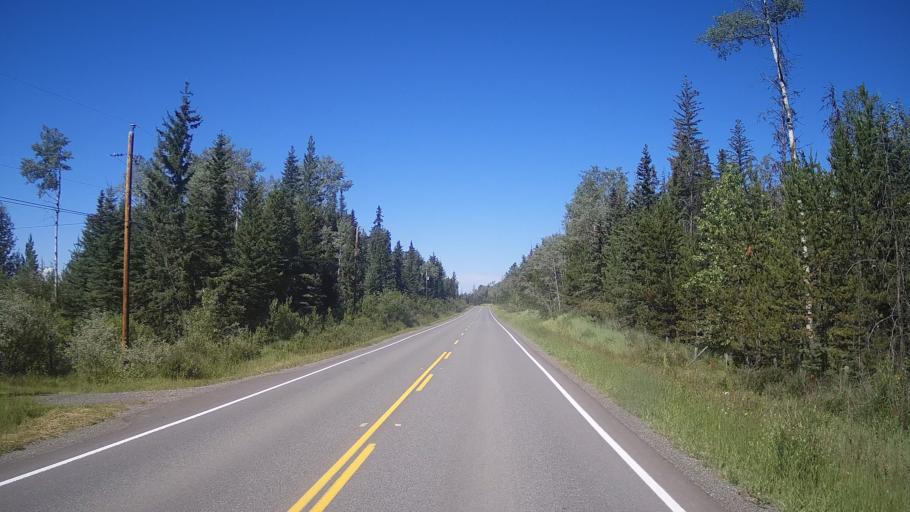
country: CA
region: British Columbia
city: Cache Creek
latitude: 51.5475
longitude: -121.0834
